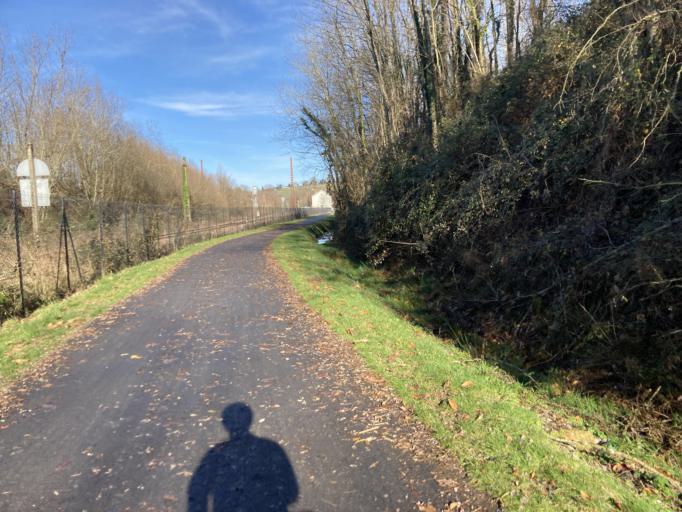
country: FR
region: Aquitaine
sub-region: Departement des Pyrenees-Atlantiques
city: Arudy
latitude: 43.1456
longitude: -0.4571
